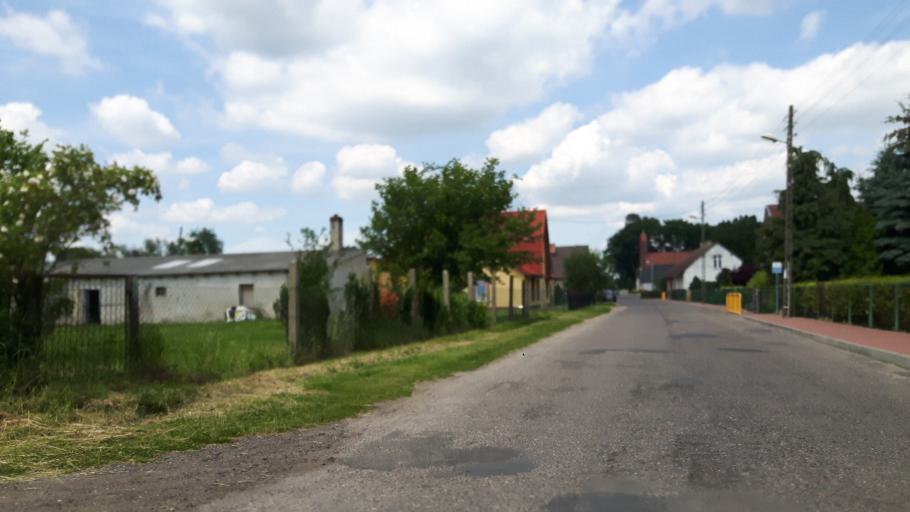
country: PL
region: West Pomeranian Voivodeship
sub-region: Powiat goleniowski
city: Osina
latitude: 53.6778
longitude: 15.0004
